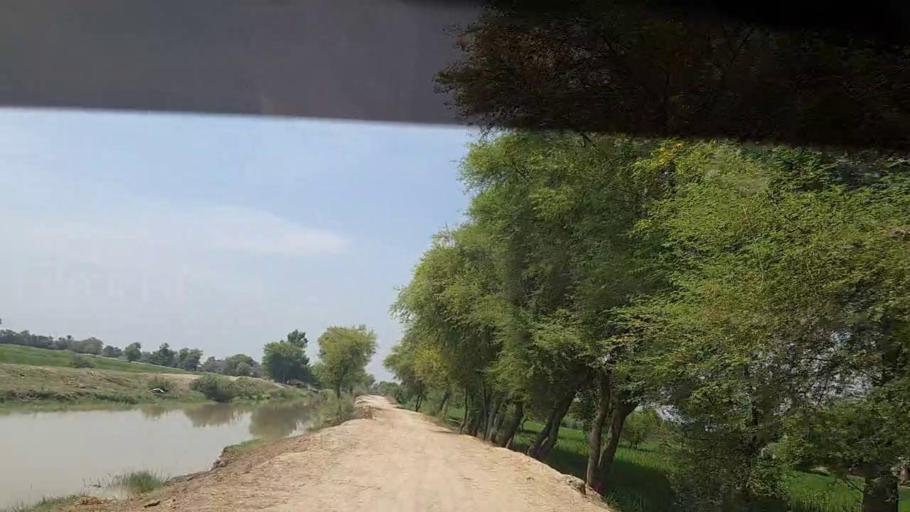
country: PK
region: Sindh
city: Thul
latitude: 28.2016
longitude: 68.6993
